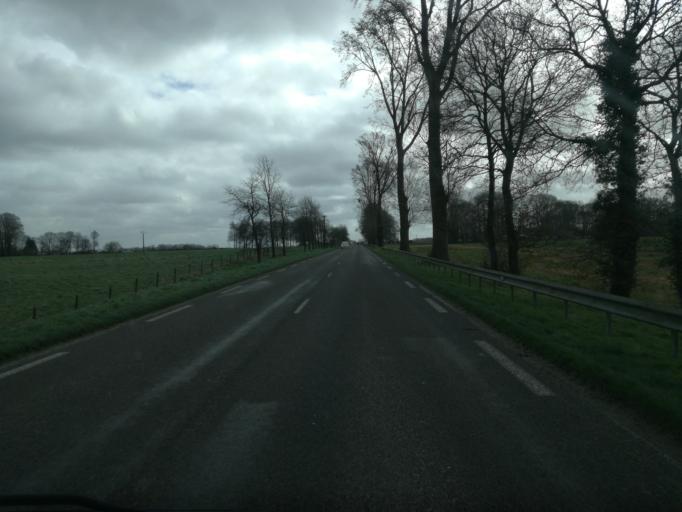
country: FR
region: Haute-Normandie
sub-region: Departement de la Seine-Maritime
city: Valliquerville
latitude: 49.6210
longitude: 0.6529
